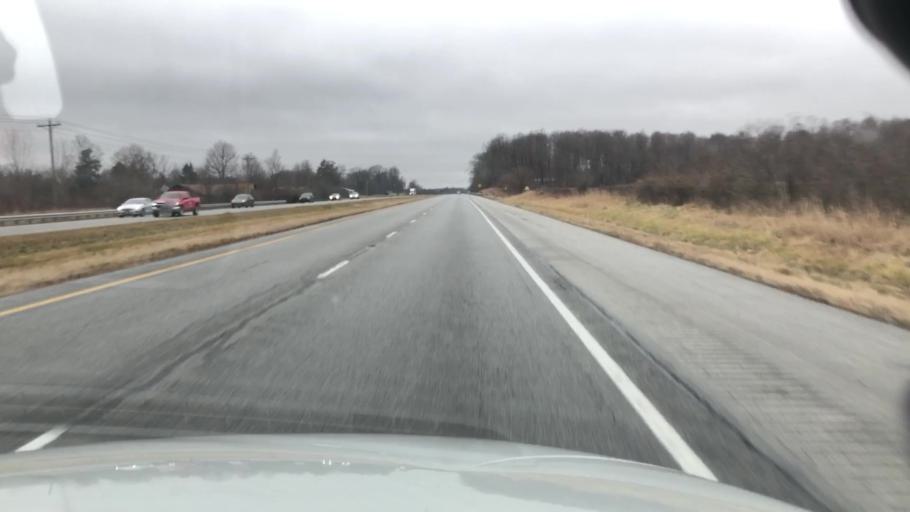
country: US
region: Indiana
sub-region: Whitley County
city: Columbia City
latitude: 41.1778
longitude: -85.5822
